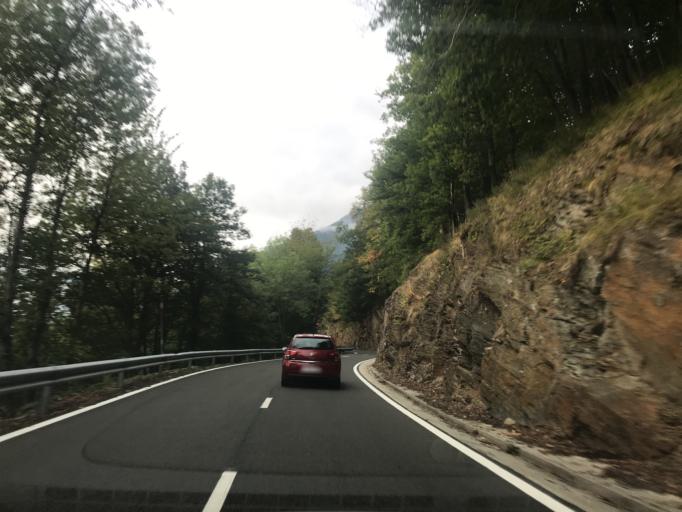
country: ES
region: Catalonia
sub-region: Provincia de Lleida
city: Les
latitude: 42.7756
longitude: 0.6778
